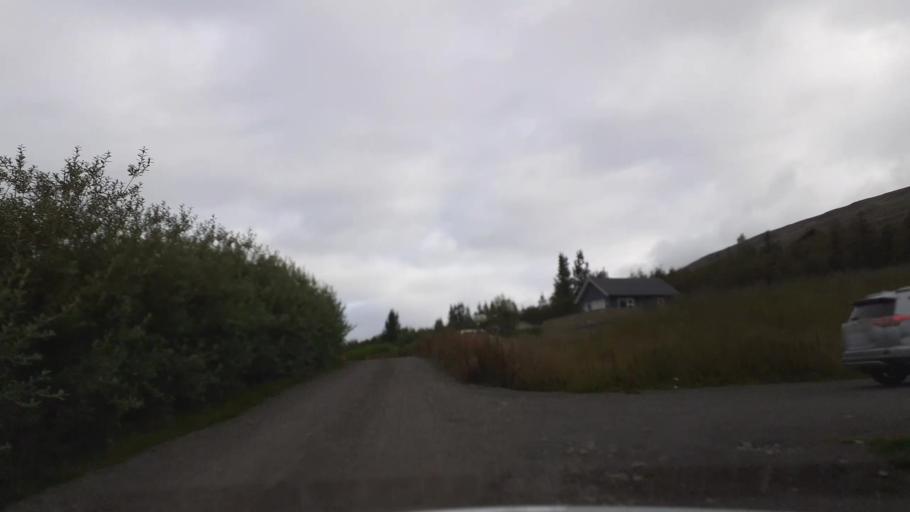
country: IS
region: Northeast
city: Akureyri
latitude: 65.6772
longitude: -18.0412
